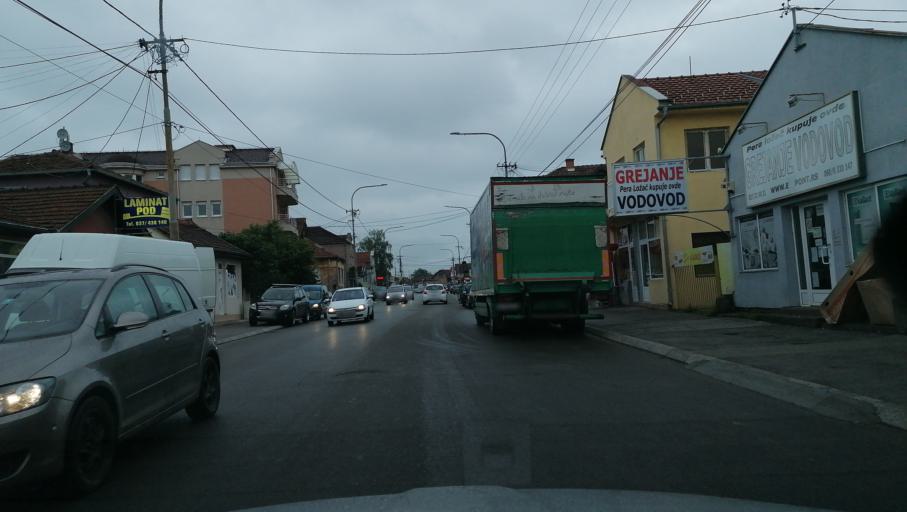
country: RS
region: Central Serbia
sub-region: Rasinski Okrug
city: Krusevac
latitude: 43.5834
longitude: 21.3102
